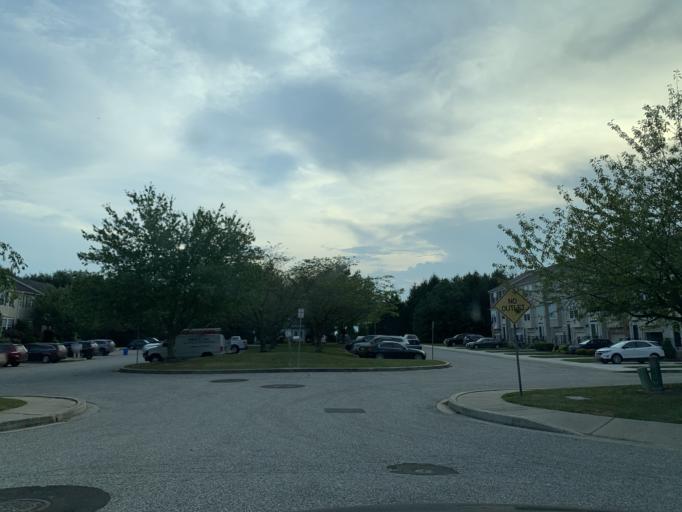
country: US
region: Maryland
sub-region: Harford County
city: Bel Air North
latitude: 39.5641
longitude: -76.3717
